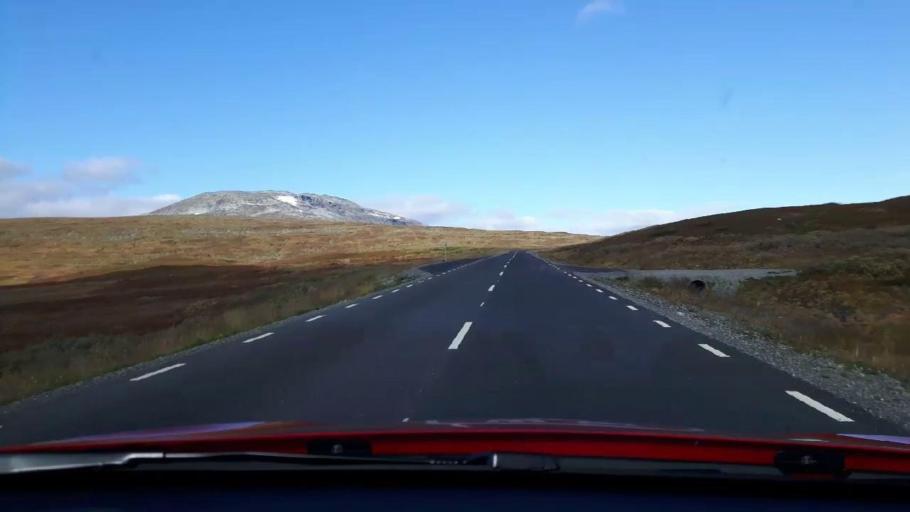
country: NO
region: Nordland
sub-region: Hattfjelldal
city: Hattfjelldal
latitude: 65.0347
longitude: 14.3315
